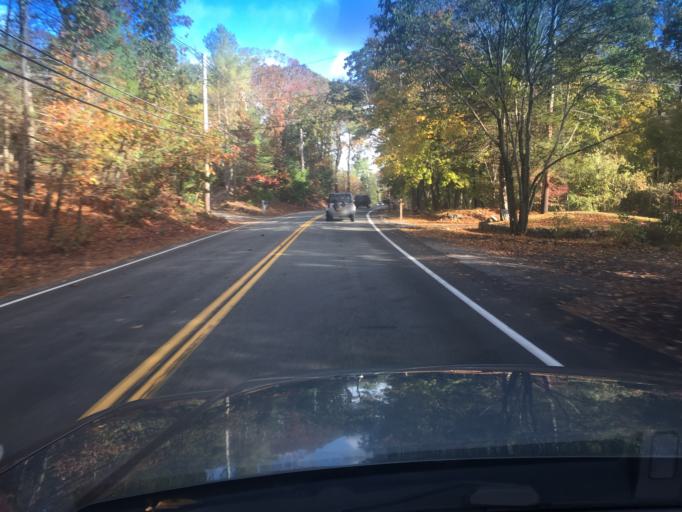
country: US
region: Massachusetts
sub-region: Norfolk County
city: Dover
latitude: 42.2320
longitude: -71.2875
